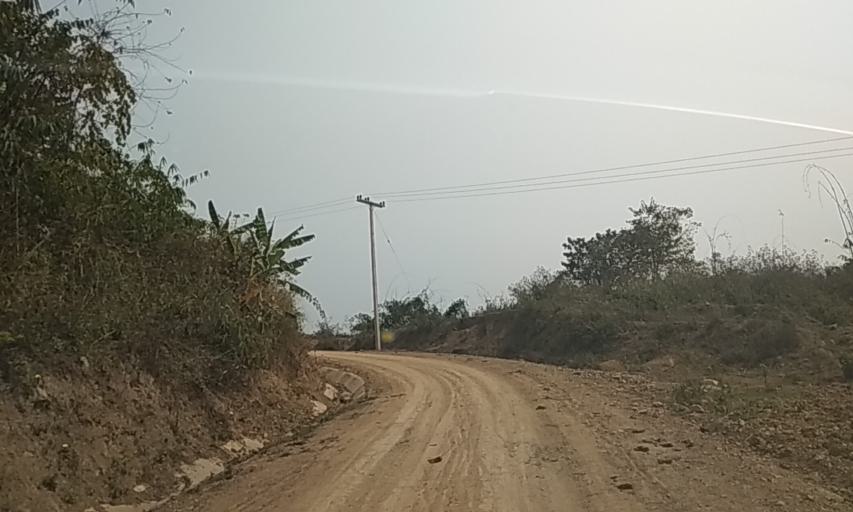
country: VN
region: Huyen Dien Bien
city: Dien Bien Phu
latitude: 21.4409
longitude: 102.7659
